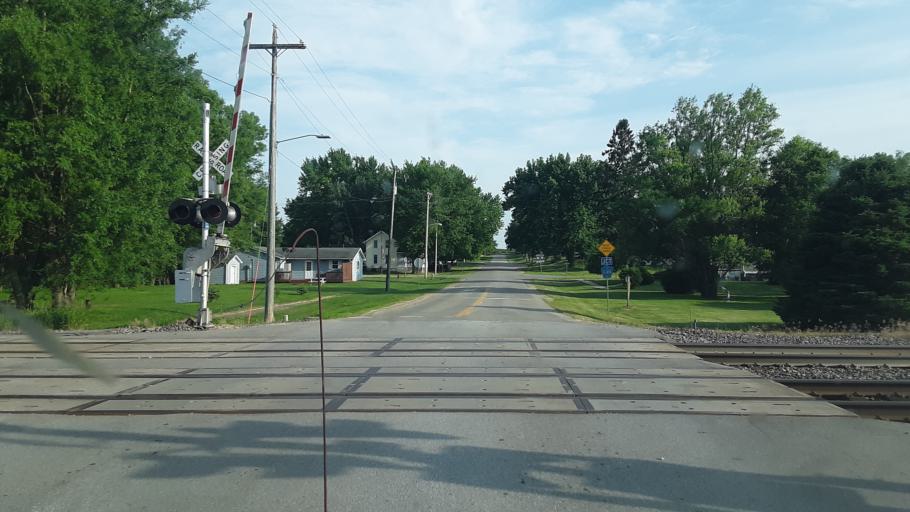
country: US
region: Iowa
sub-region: Tama County
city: Tama
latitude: 41.9806
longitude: -92.7148
